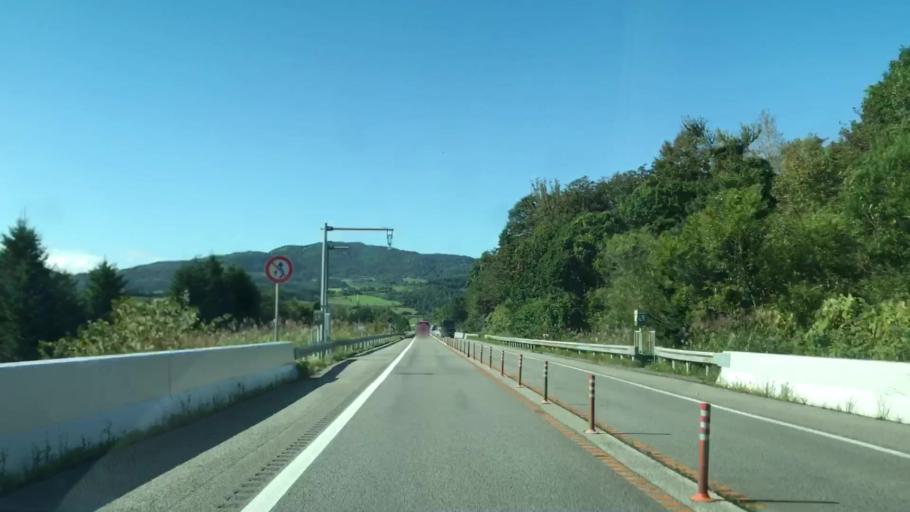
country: JP
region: Hokkaido
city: Date
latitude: 42.5354
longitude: 140.7979
